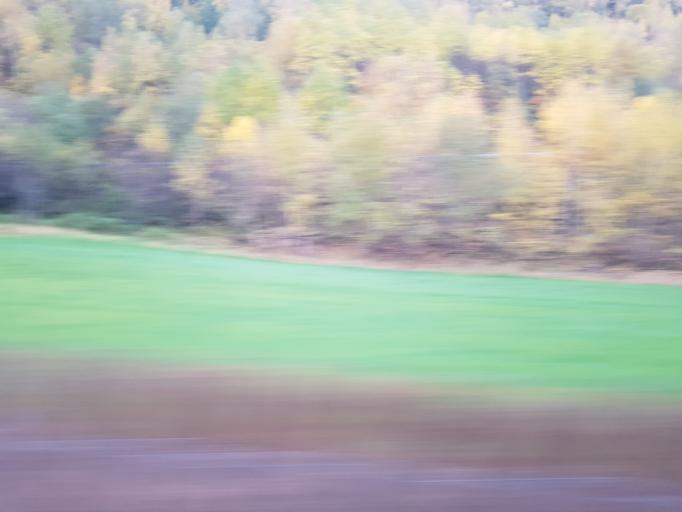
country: NO
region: Oppland
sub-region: Sel
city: Otta
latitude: 61.8333
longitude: 9.4893
